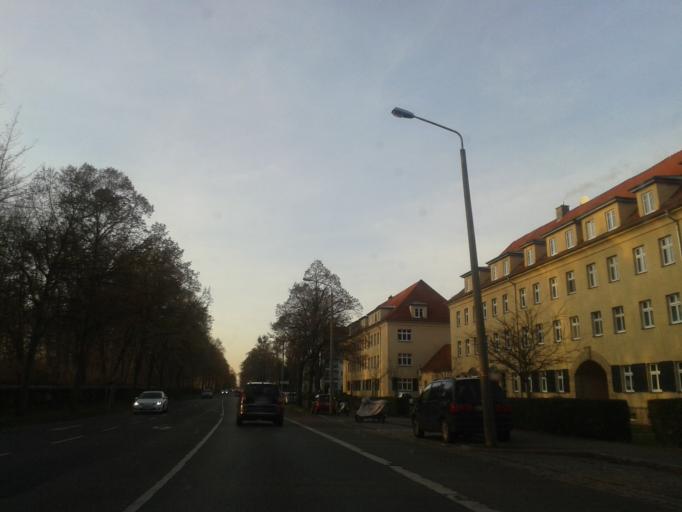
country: DE
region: Saxony
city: Dresden
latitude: 51.0220
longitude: 13.8029
